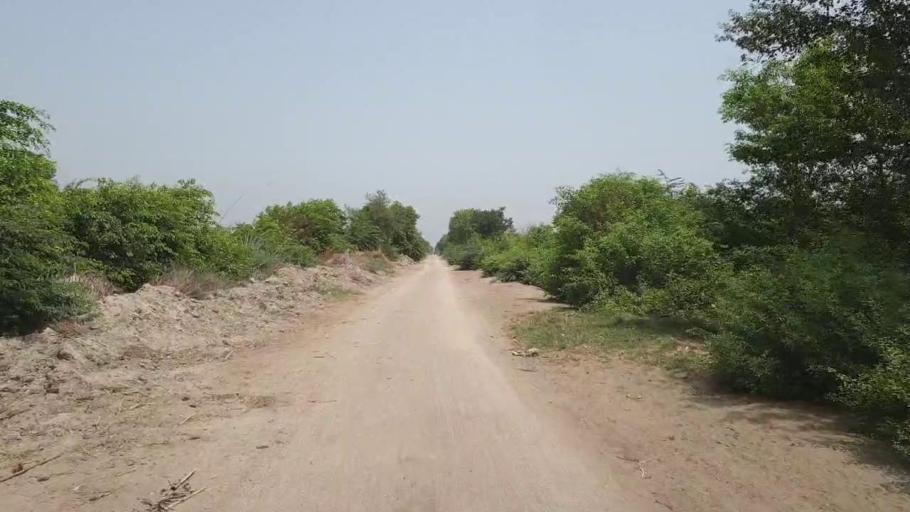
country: PK
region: Sindh
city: Nawabshah
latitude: 26.3064
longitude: 68.3030
